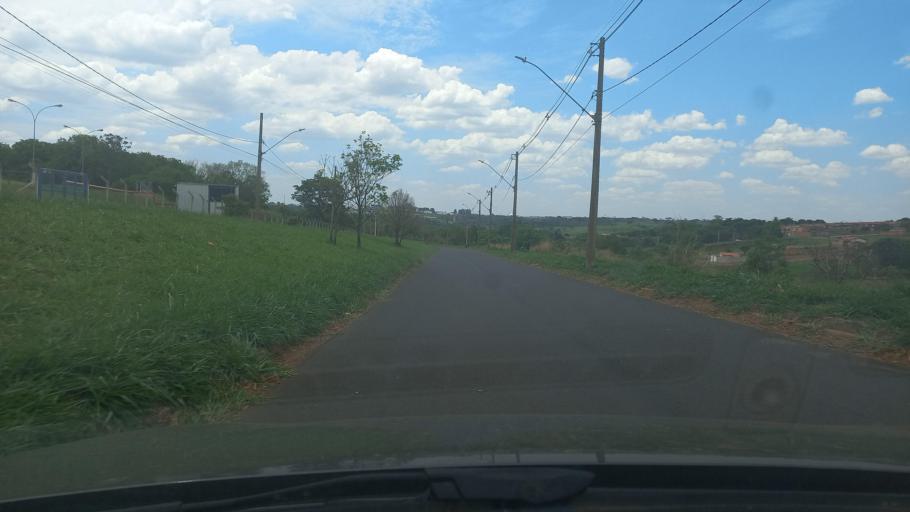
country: BR
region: Minas Gerais
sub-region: Uberaba
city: Uberaba
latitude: -19.7382
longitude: -47.9742
